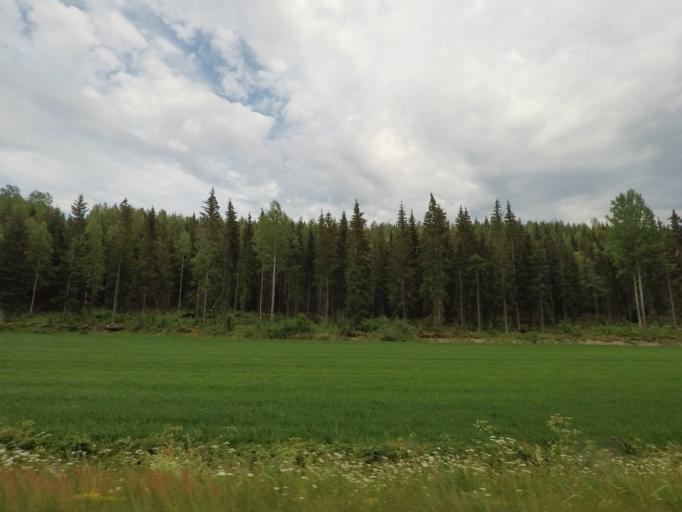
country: FI
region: Uusimaa
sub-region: Porvoo
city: Pukkila
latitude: 60.7903
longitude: 25.4649
